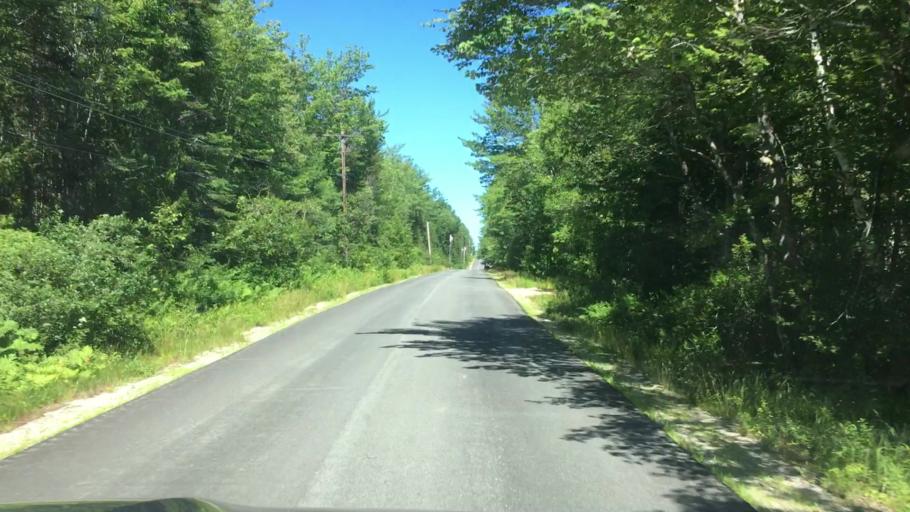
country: US
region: Maine
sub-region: Hancock County
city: Sedgwick
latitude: 44.3166
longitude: -68.6209
